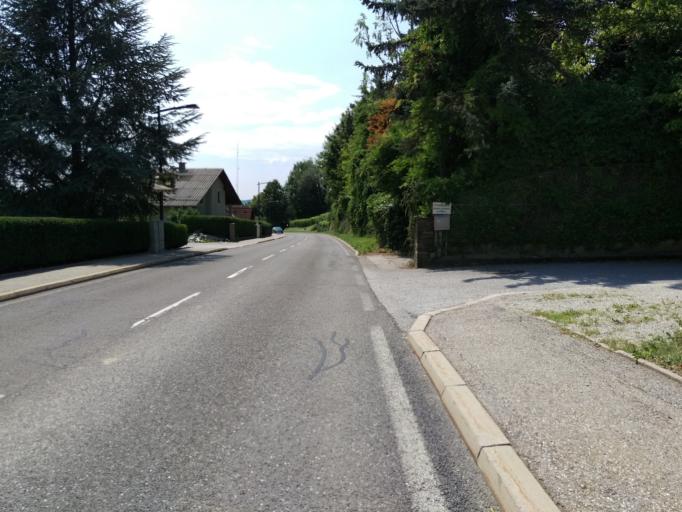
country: AT
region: Styria
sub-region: Politischer Bezirk Graz-Umgebung
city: Nestelbach bei Graz
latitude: 47.0682
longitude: 15.5882
